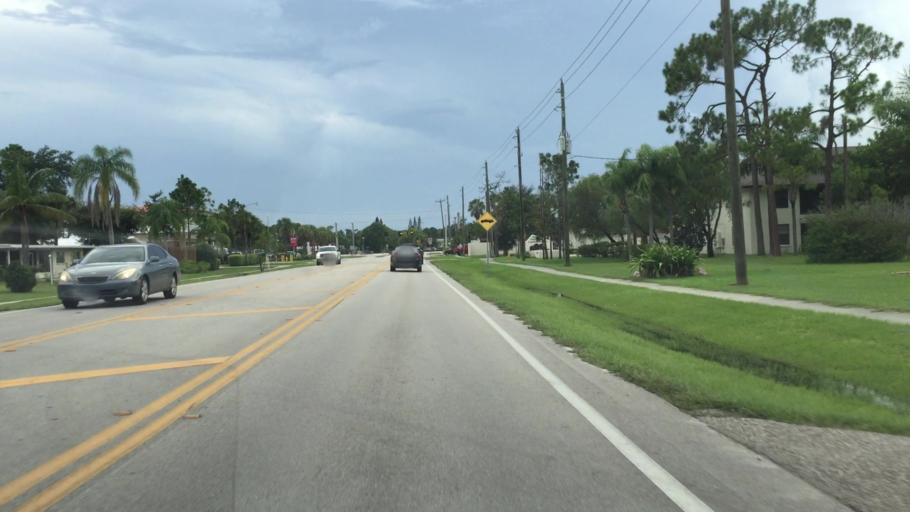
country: US
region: Florida
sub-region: Lee County
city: Pine Manor
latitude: 26.5646
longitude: -81.8691
